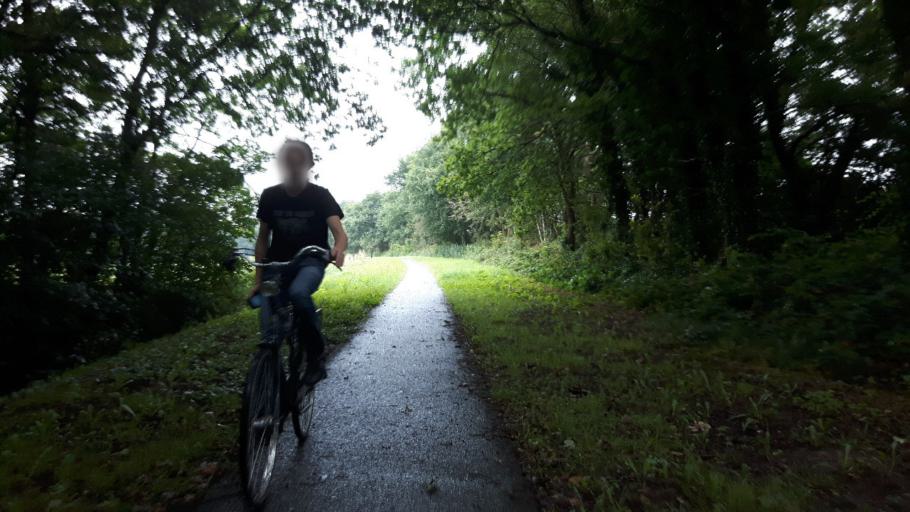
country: NL
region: Overijssel
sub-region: Gemeente Steenwijkerland
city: Oldemarkt
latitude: 52.8012
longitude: 5.9887
